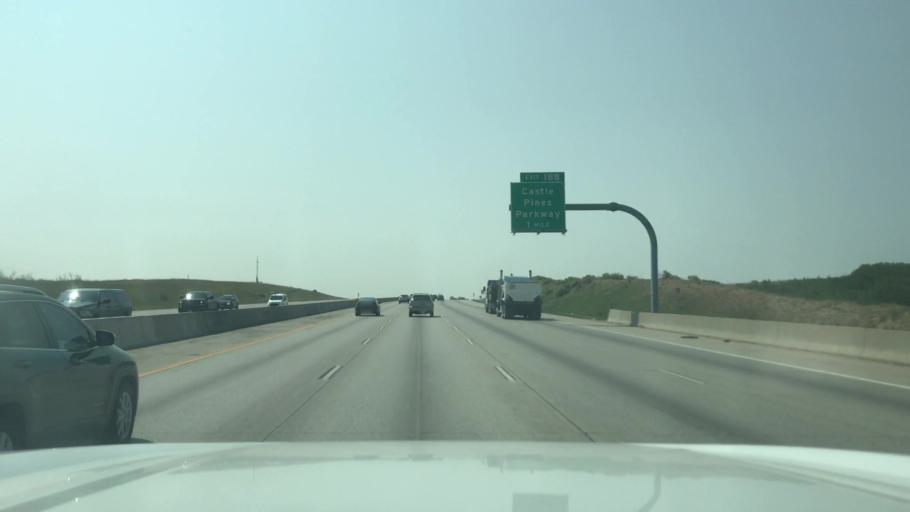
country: US
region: Colorado
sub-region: Park County
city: Castle Pines North
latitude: 39.4893
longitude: -104.8729
